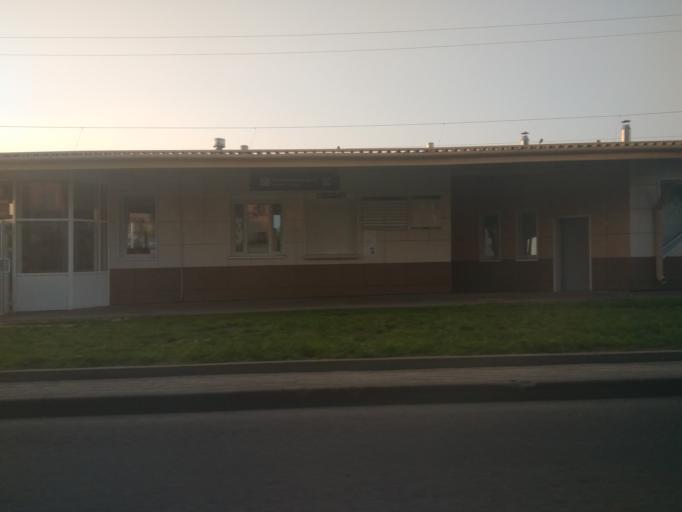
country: BY
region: Minsk
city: Novoye Medvezhino
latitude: 53.9297
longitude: 27.4775
